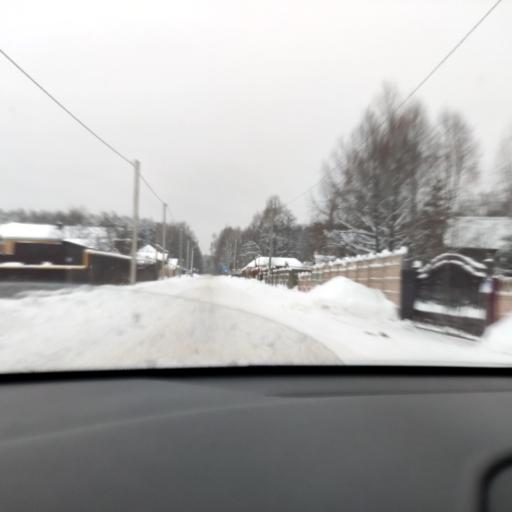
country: RU
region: Tatarstan
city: Vysokaya Gora
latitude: 55.9550
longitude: 49.1603
